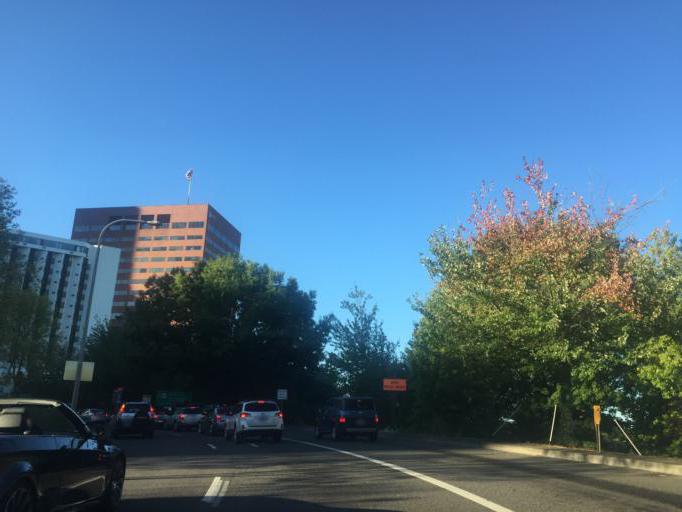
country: US
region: Oregon
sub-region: Multnomah County
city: Portland
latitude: 45.5113
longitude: -122.6750
